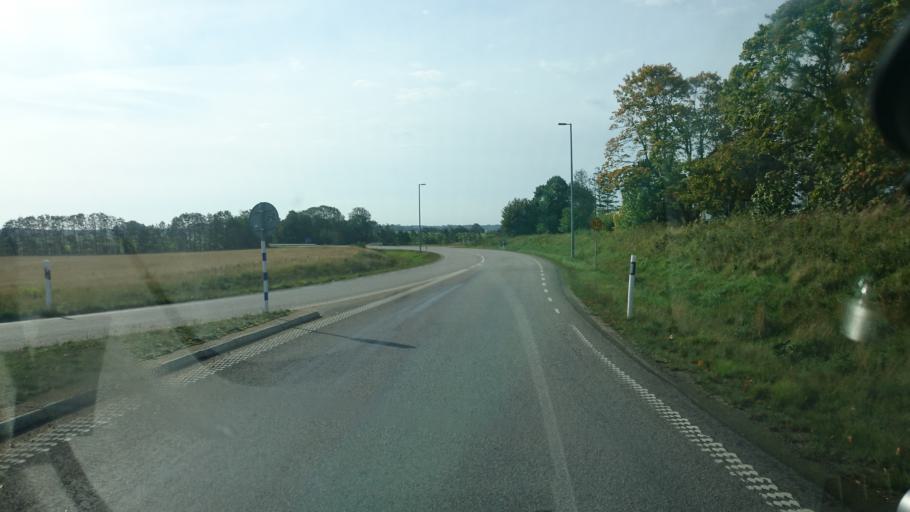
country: SE
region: Vaestra Goetaland
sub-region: Vanersborgs Kommun
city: Vargon
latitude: 58.2903
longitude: 12.3942
